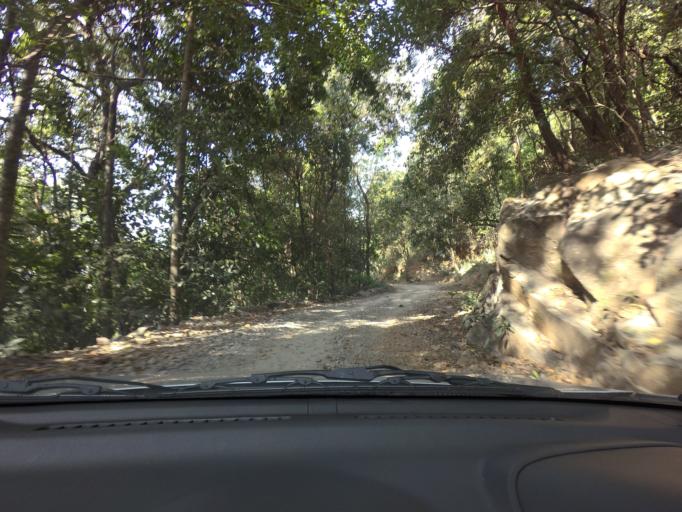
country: IN
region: Karnataka
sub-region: Kodagu
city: Somvarpet
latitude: 12.7114
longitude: 75.6715
